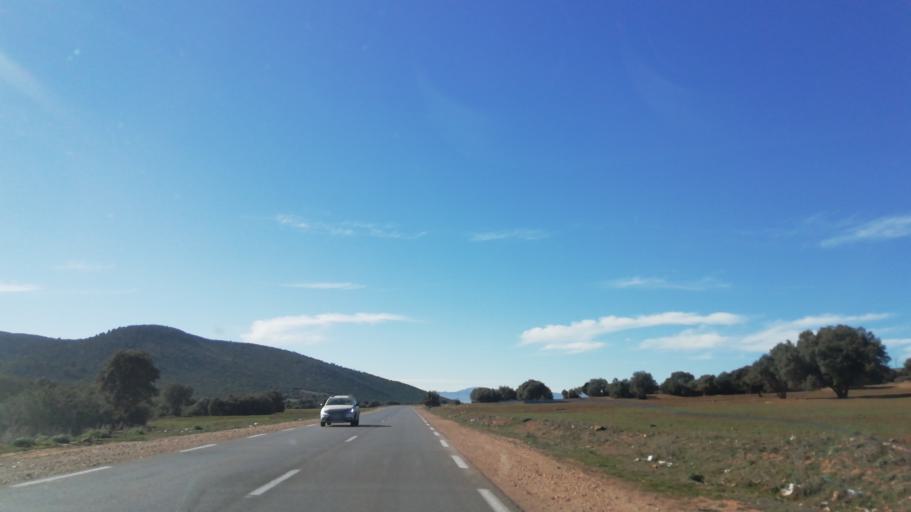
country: DZ
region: Tlemcen
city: Sebdou
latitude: 34.7075
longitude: -1.2152
